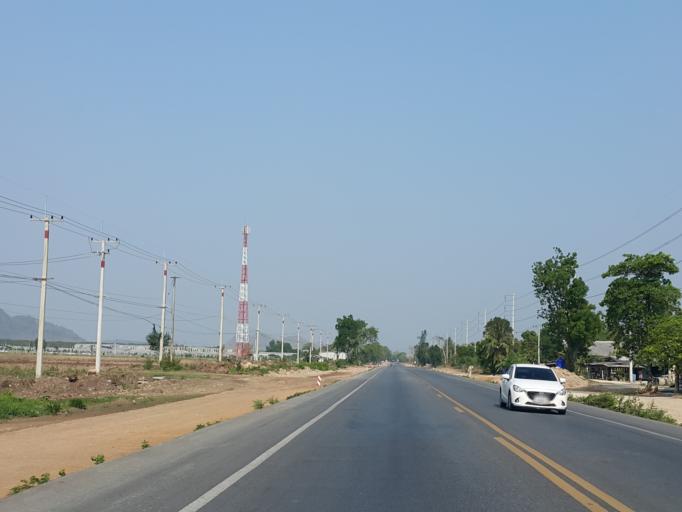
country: TH
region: Kanchanaburi
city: Sai Yok
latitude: 14.0884
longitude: 99.3277
